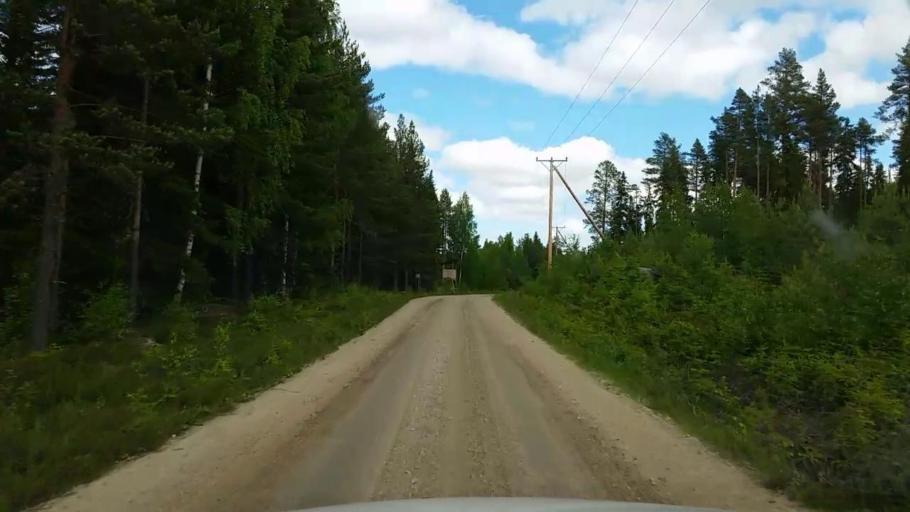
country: SE
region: Gaevleborg
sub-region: Ovanakers Kommun
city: Edsbyn
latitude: 61.5284
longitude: 15.9451
